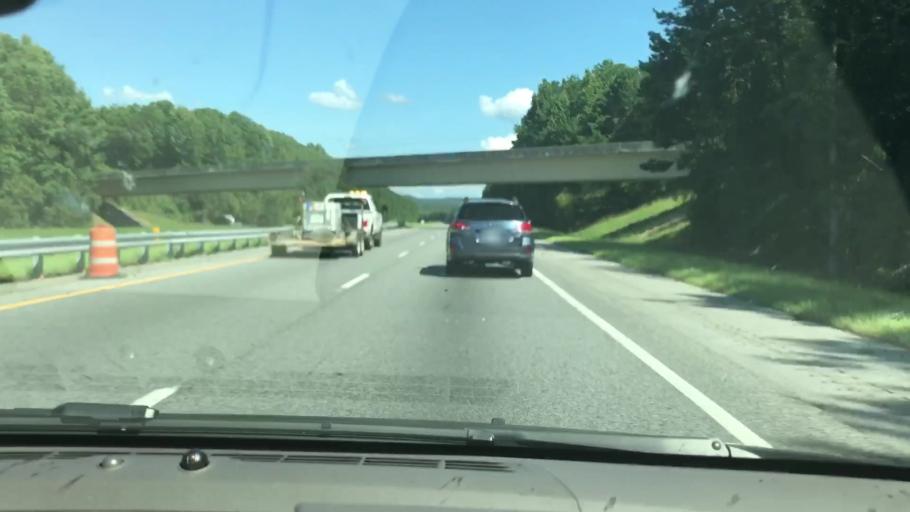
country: US
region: Georgia
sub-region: Harris County
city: Hamilton
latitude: 32.6779
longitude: -84.9890
